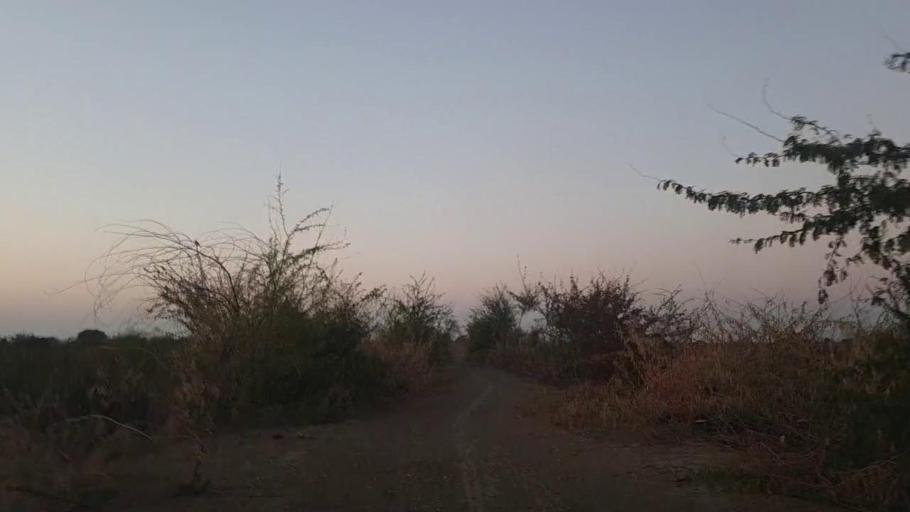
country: PK
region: Sindh
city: Tando Mittha Khan
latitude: 26.0835
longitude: 69.1508
